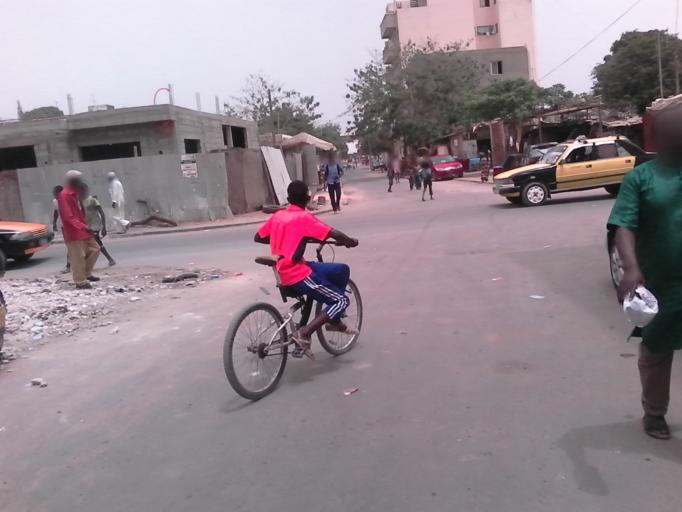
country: SN
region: Dakar
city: Grand Dakar
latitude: 14.7041
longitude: -17.4540
